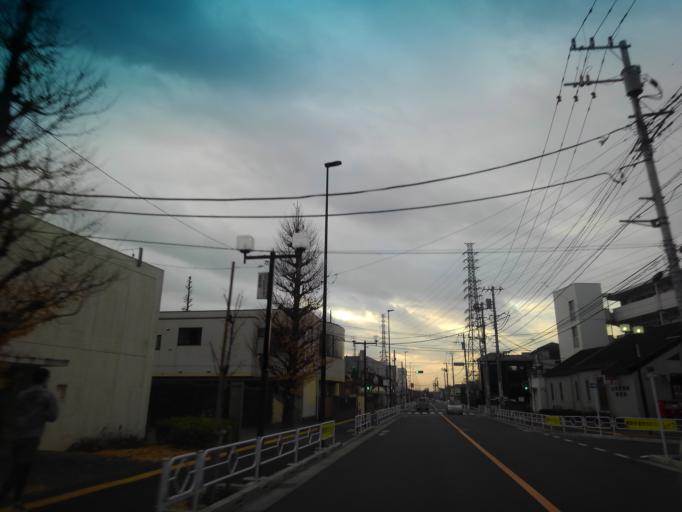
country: JP
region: Tokyo
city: Kokubunji
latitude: 35.7229
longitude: 139.4429
